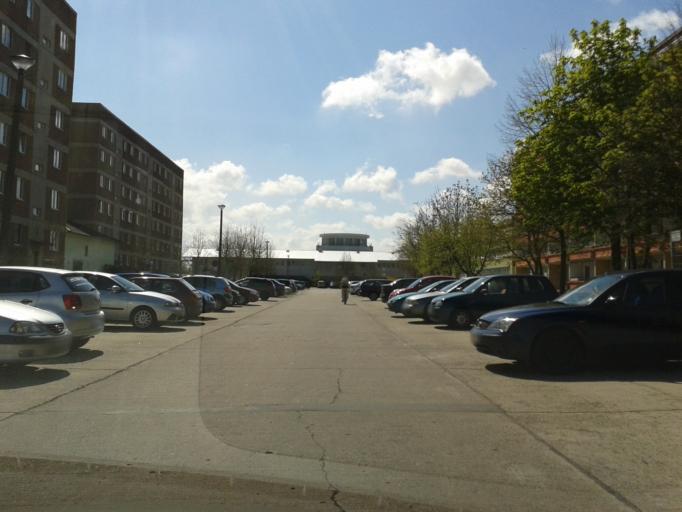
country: DE
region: Saxony-Anhalt
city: Salzwedel
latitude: 52.8458
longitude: 11.1707
